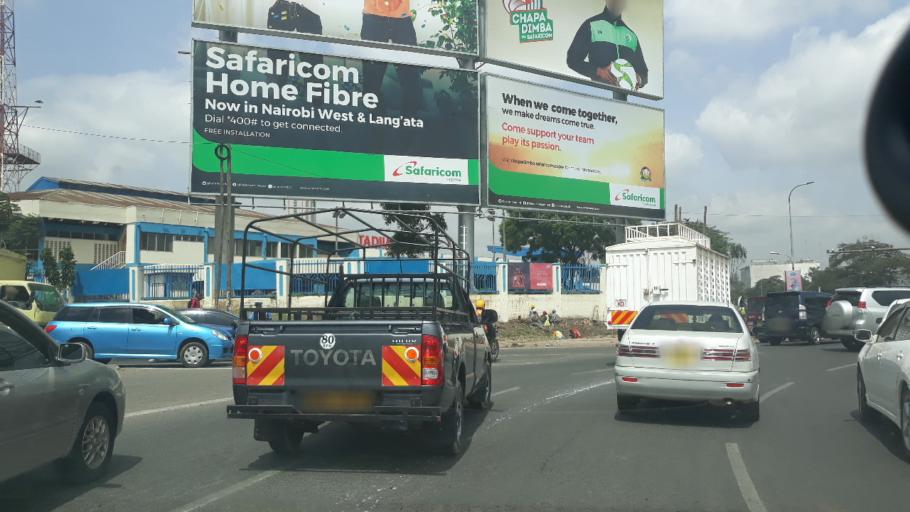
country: KE
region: Nairobi Area
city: Nairobi
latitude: -1.3051
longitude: 36.8263
